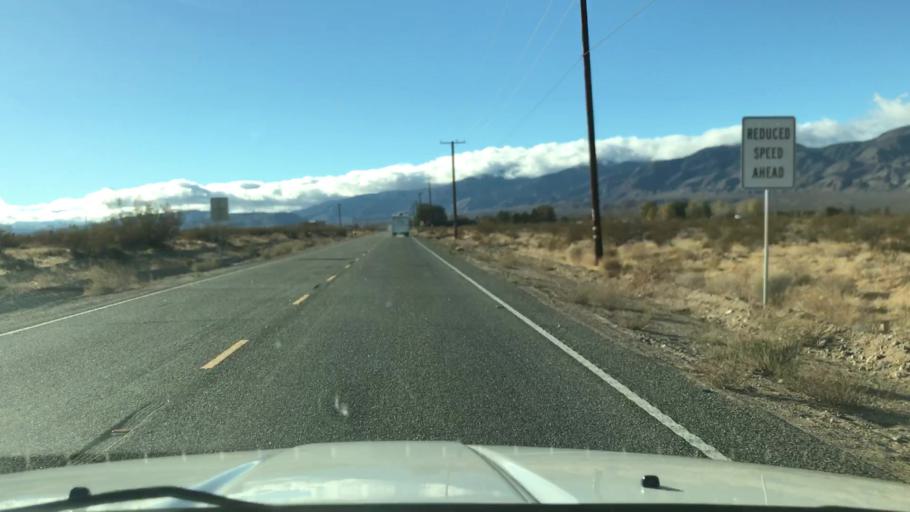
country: US
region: California
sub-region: Kern County
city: Mojave
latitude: 35.1255
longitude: -118.1067
